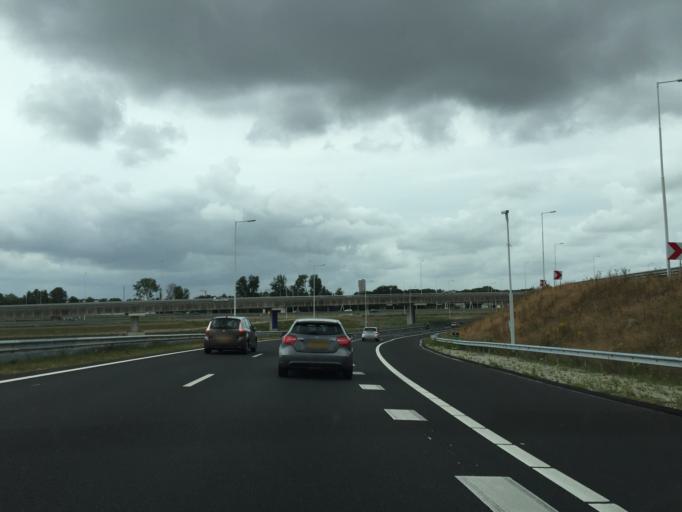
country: NL
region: South Holland
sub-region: Gemeente Albrandswaard
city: Rhoon
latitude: 51.8757
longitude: 4.3830
